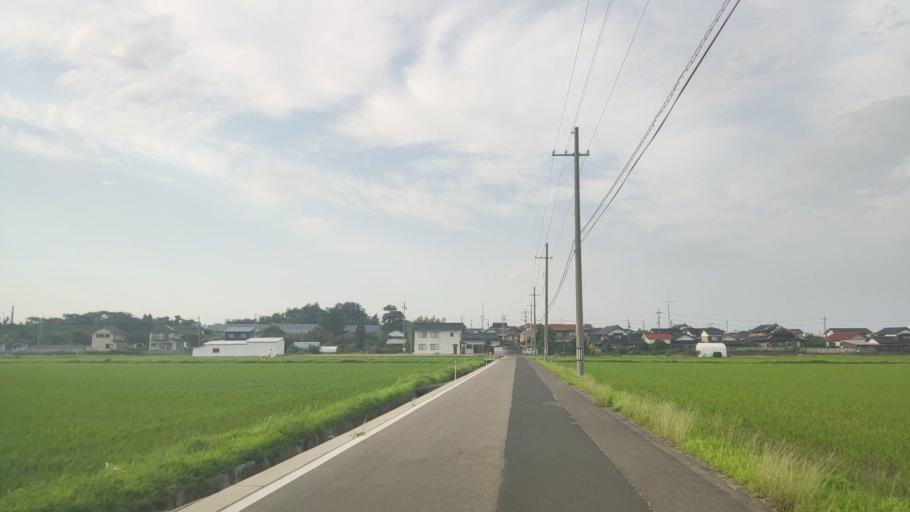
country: JP
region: Tottori
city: Kurayoshi
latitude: 35.4862
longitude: 133.8136
